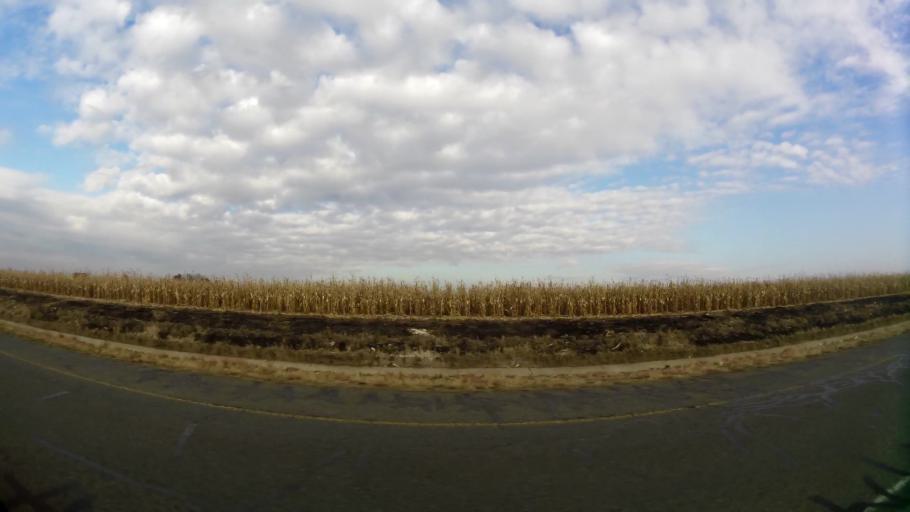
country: ZA
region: Gauteng
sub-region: Sedibeng District Municipality
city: Vanderbijlpark
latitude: -26.6472
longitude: 27.7788
